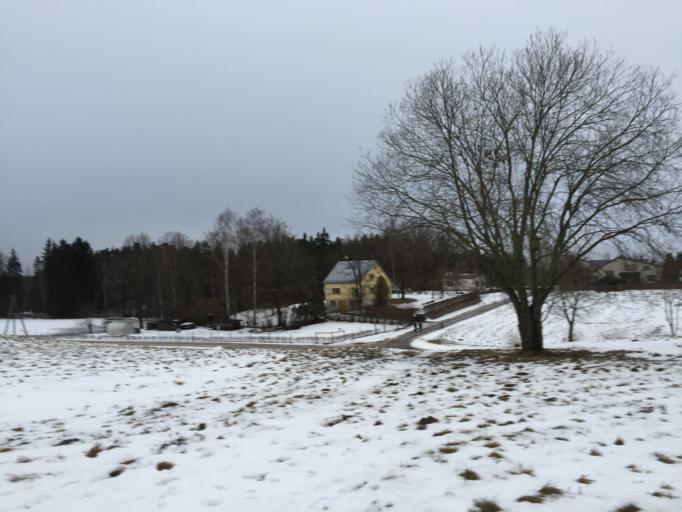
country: LV
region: Krimulda
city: Ragana
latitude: 57.1830
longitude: 24.6965
